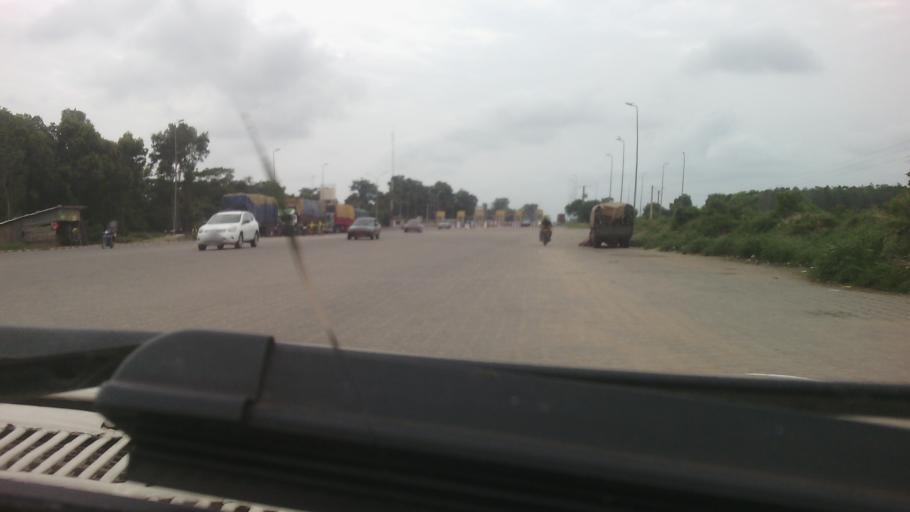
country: BJ
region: Atlantique
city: Ouidah
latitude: 6.3724
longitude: 2.1418
